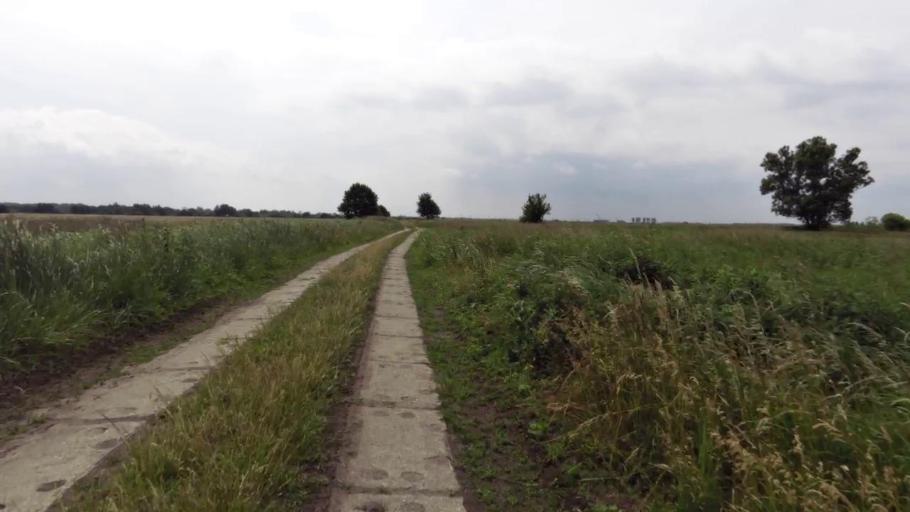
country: PL
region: West Pomeranian Voivodeship
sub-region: Powiat goleniowski
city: Stepnica
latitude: 53.7468
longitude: 14.6239
